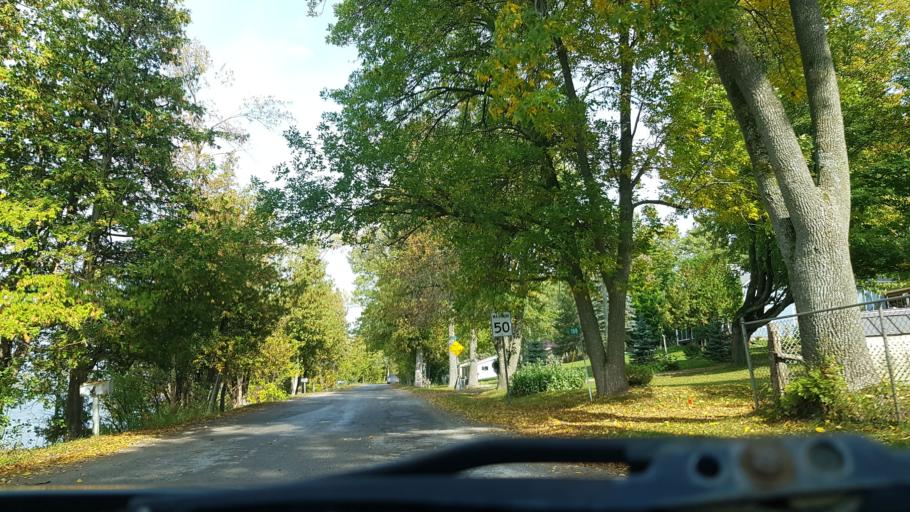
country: CA
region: Ontario
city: Orillia
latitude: 44.6557
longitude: -79.1021
